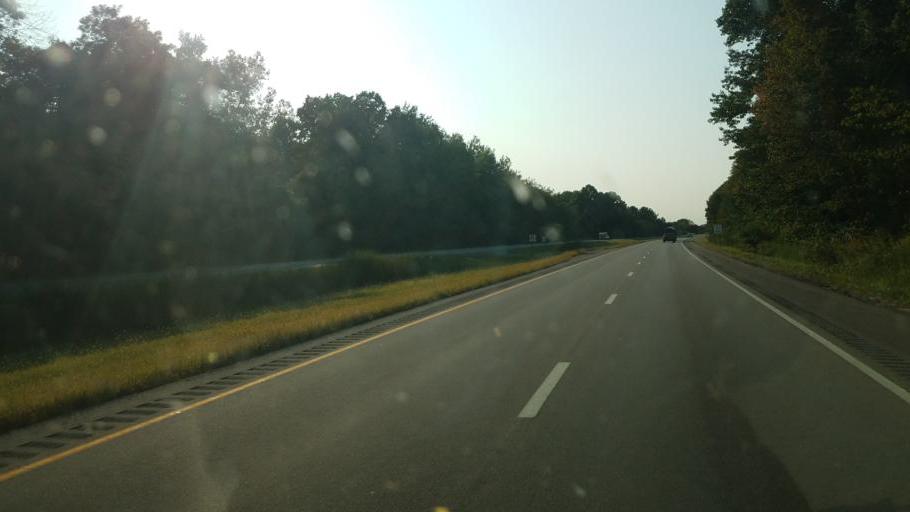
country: US
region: Ohio
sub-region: Stark County
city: Brewster
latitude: 40.7729
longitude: -81.5893
